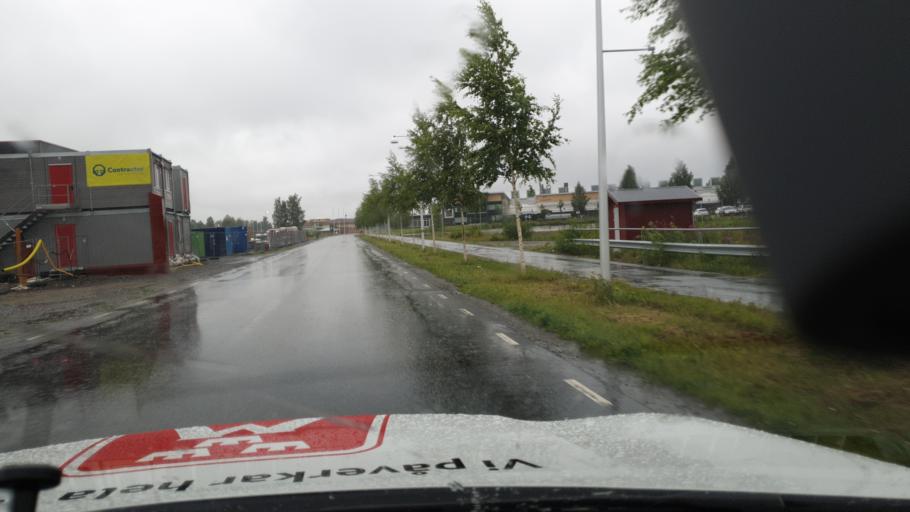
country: SE
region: Vaesterbotten
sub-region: Skelleftea Kommun
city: Skelleftea
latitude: 64.7326
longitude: 20.9752
